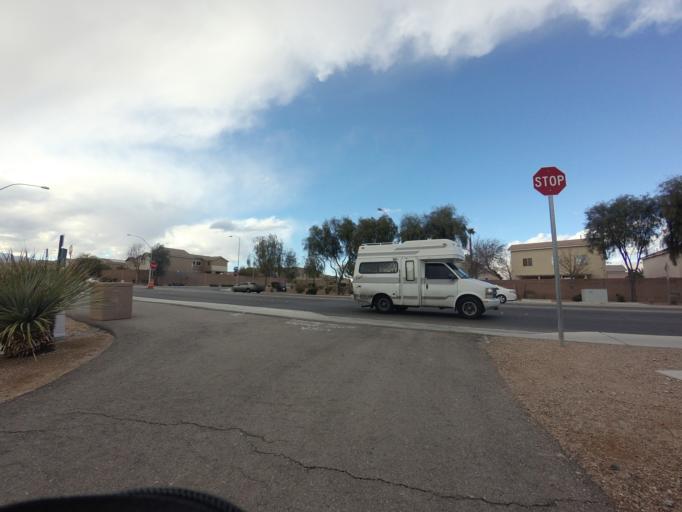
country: US
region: Nevada
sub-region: Clark County
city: North Las Vegas
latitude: 36.2688
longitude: -115.1972
